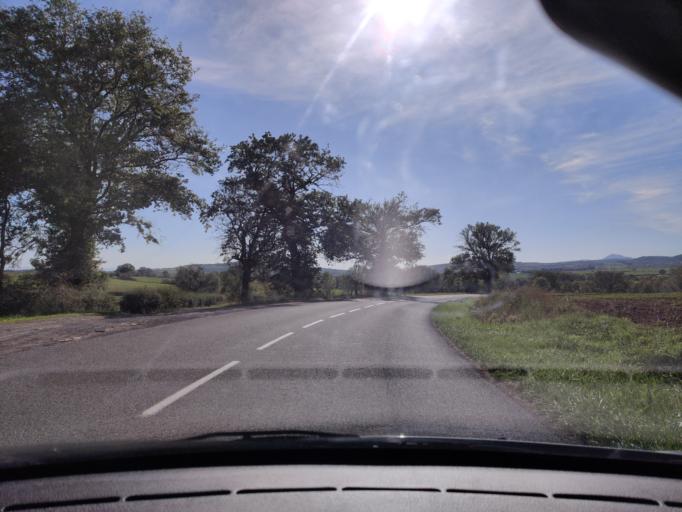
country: FR
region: Auvergne
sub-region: Departement du Puy-de-Dome
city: Combronde
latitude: 46.0150
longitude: 3.0980
